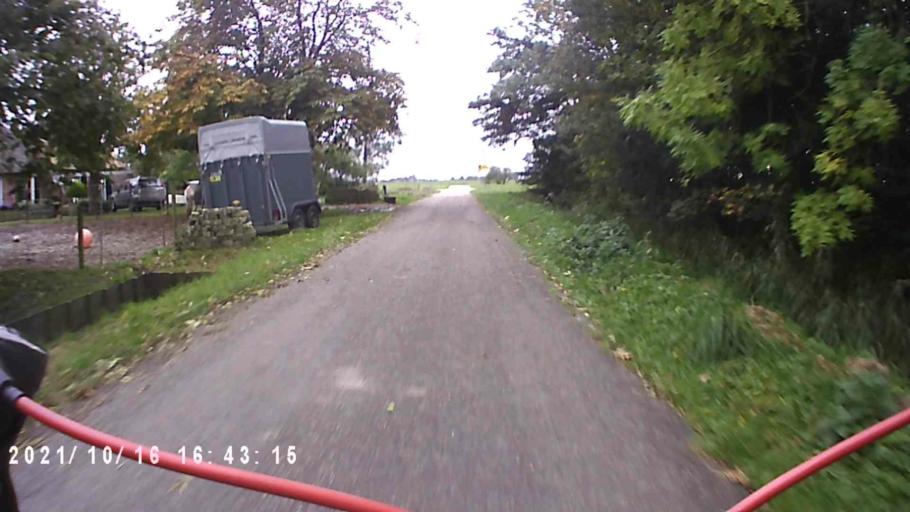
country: NL
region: Friesland
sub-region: Gemeente Dongeradeel
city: Anjum
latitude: 53.3712
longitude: 6.1432
